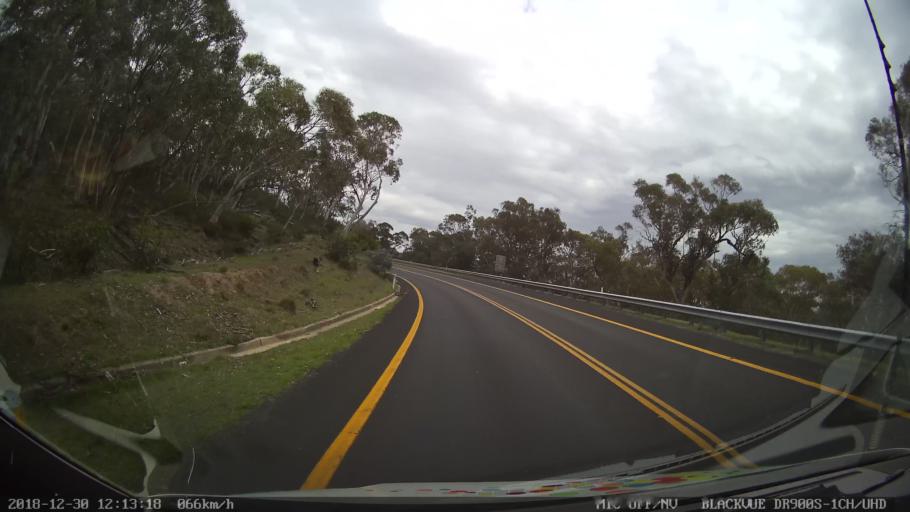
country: AU
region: New South Wales
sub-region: Snowy River
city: Jindabyne
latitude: -36.3497
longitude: 148.5856
